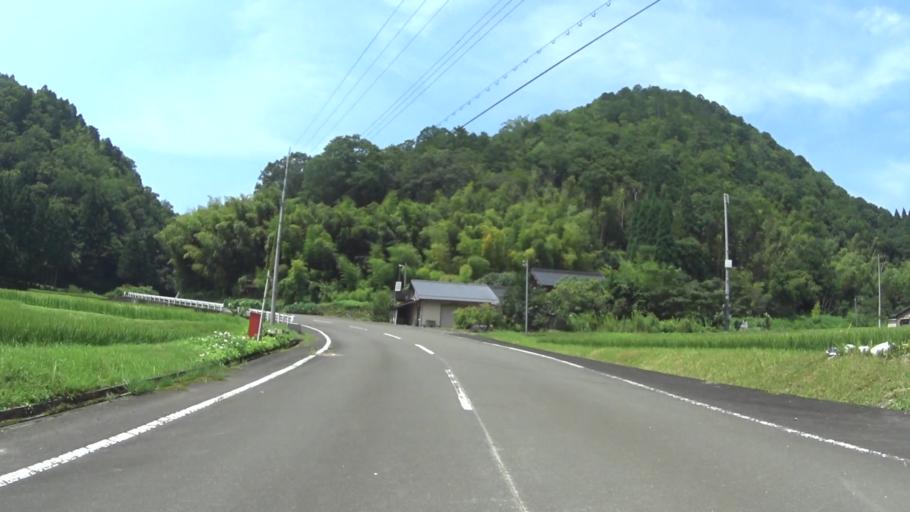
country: JP
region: Kyoto
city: Ayabe
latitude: 35.3007
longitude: 135.4160
